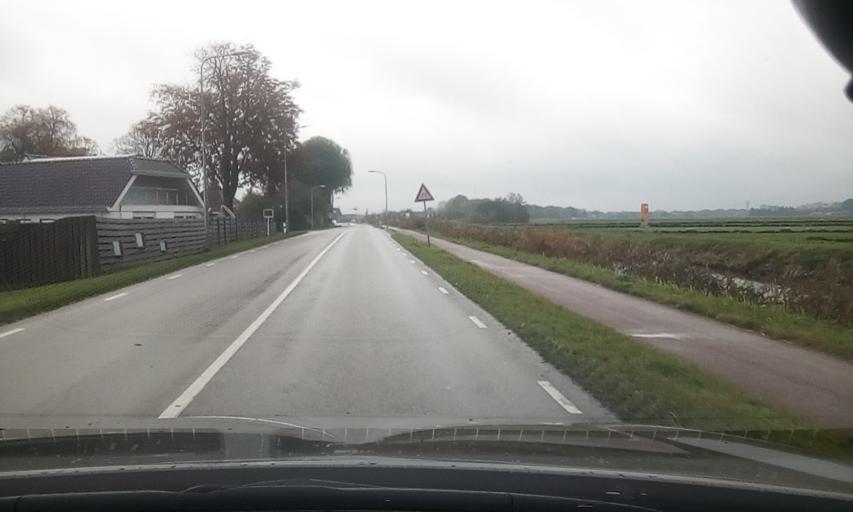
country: NL
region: Groningen
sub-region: Gemeente Groningen
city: Oosterpark
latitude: 53.2295
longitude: 6.6403
